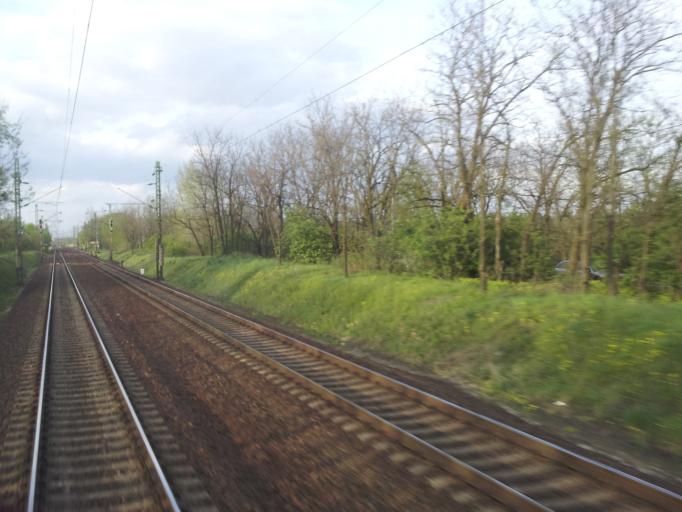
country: HU
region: Pest
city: Dunakeszi
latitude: 47.6148
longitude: 19.1319
